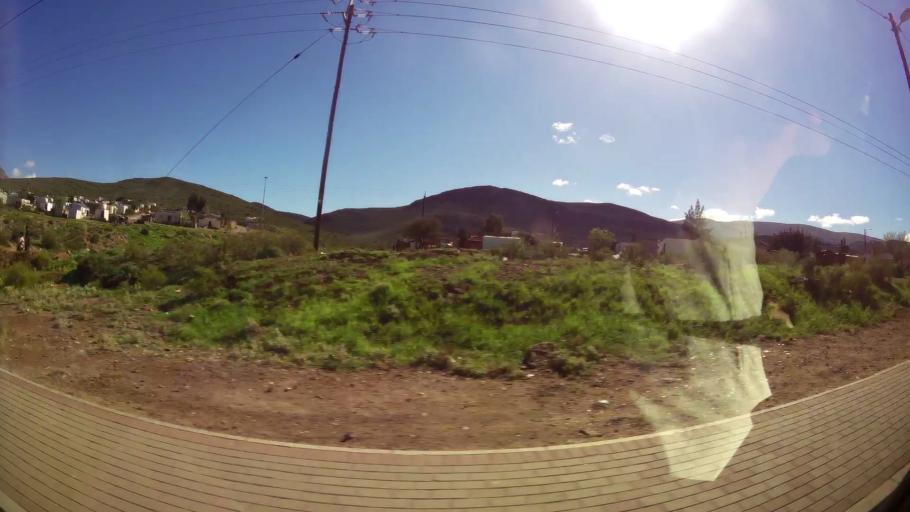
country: ZA
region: Western Cape
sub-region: Cape Winelands District Municipality
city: Ashton
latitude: -33.7693
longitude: 20.1442
